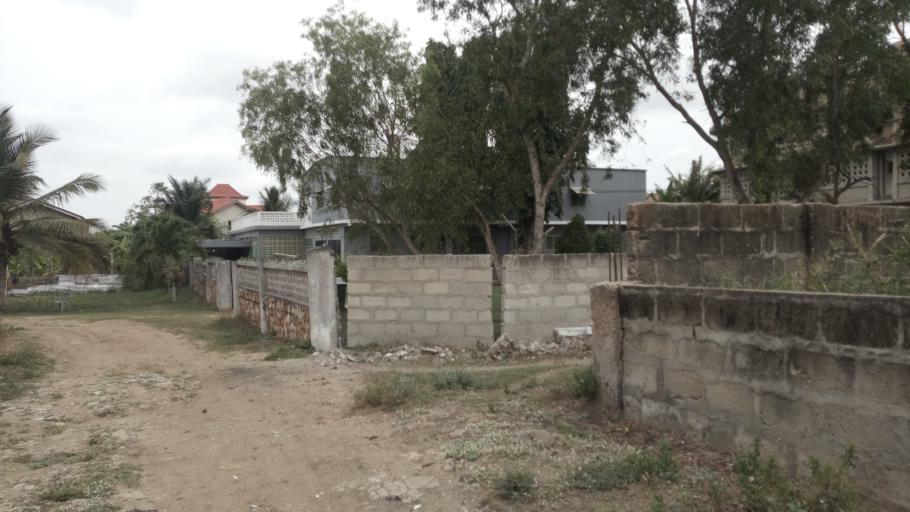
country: GH
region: Central
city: Winneba
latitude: 5.3671
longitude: -0.6395
